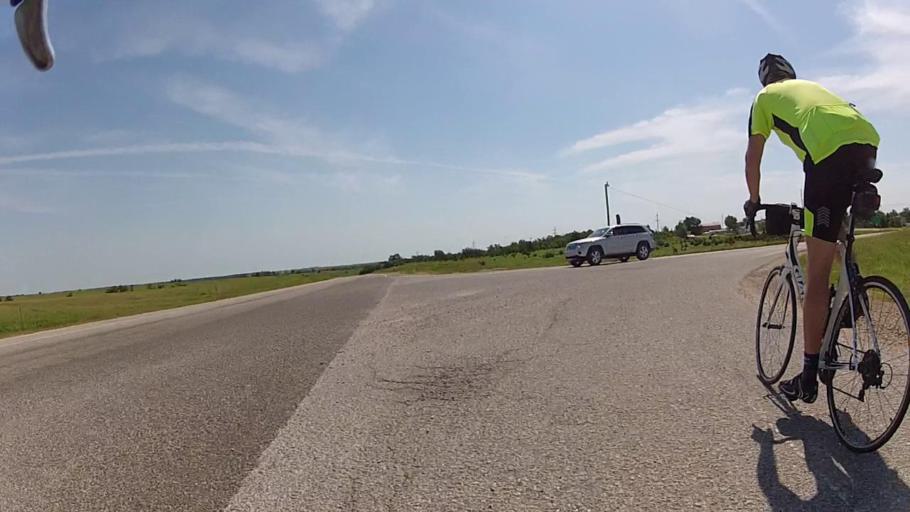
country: US
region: Kansas
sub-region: Chautauqua County
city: Sedan
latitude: 37.1114
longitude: -96.5118
